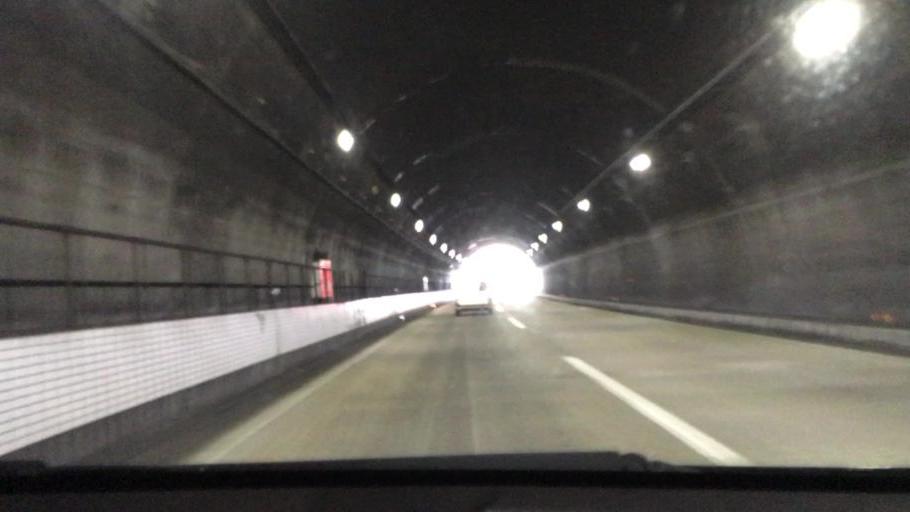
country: JP
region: Yamaguchi
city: Tokuyama
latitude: 34.0688
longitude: 131.7063
